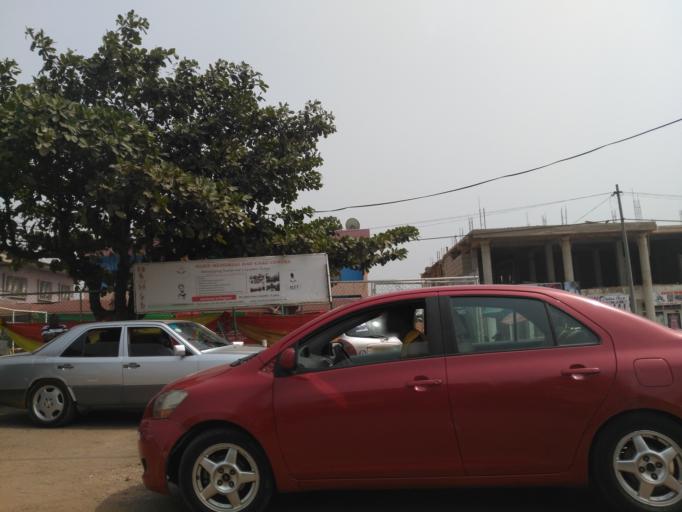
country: GH
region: Ashanti
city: Kumasi
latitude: 6.6853
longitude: -1.6444
